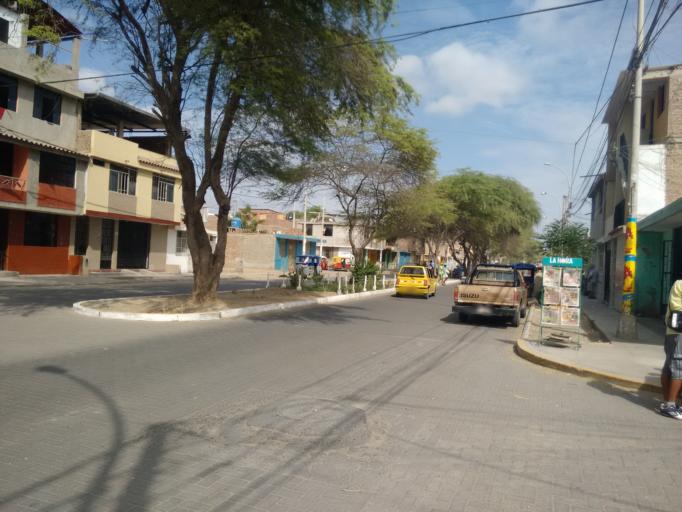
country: PE
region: Piura
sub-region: Provincia de Piura
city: Piura
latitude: -5.1772
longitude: -80.6430
